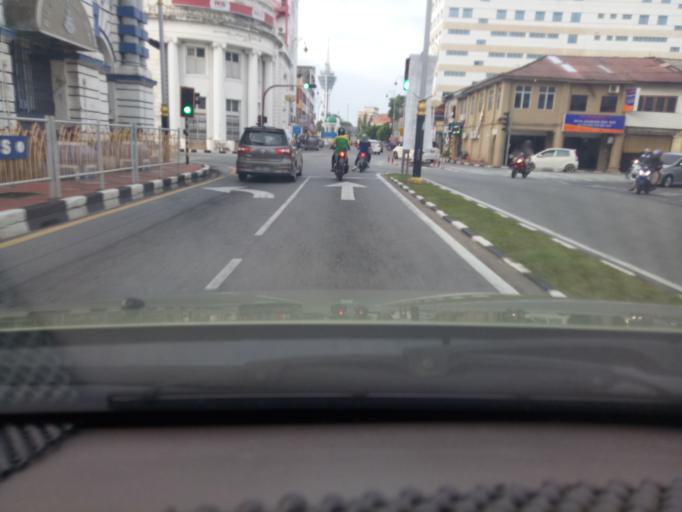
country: MY
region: Kedah
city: Alor Setar
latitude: 6.1165
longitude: 100.3654
